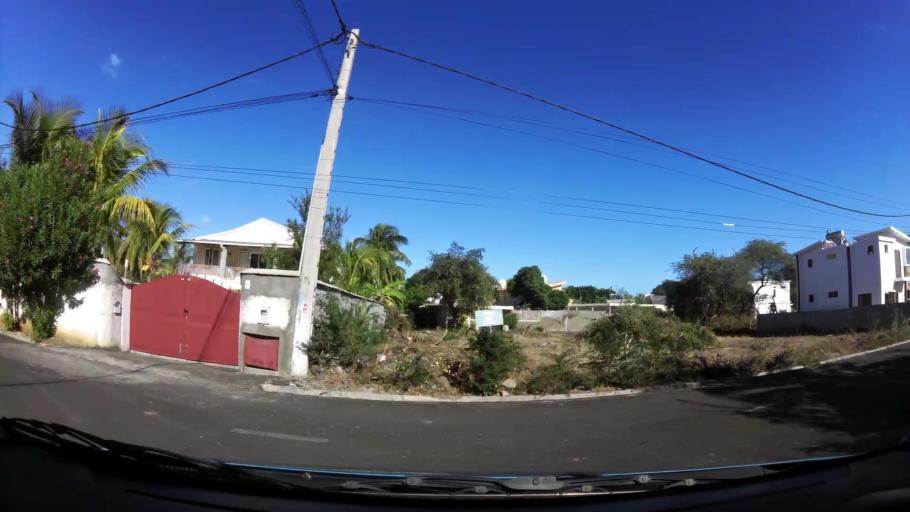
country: MU
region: Black River
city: Grande Riviere Noire
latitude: -20.3556
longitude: 57.3643
